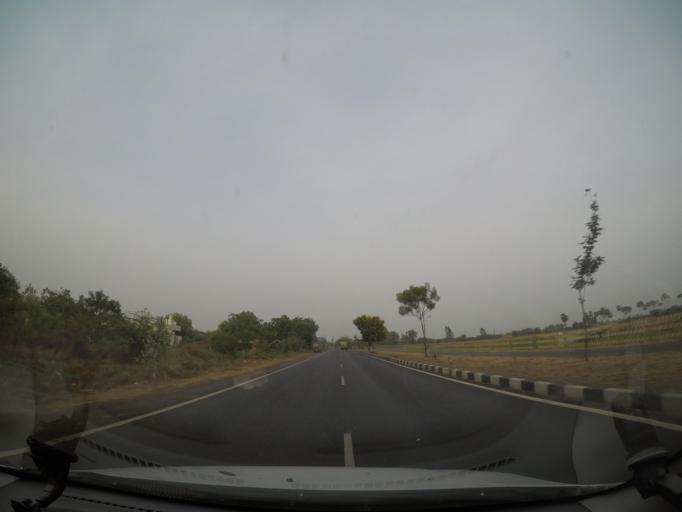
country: IN
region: Andhra Pradesh
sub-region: Krishna
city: Gannavaram
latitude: 16.6176
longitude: 80.9268
